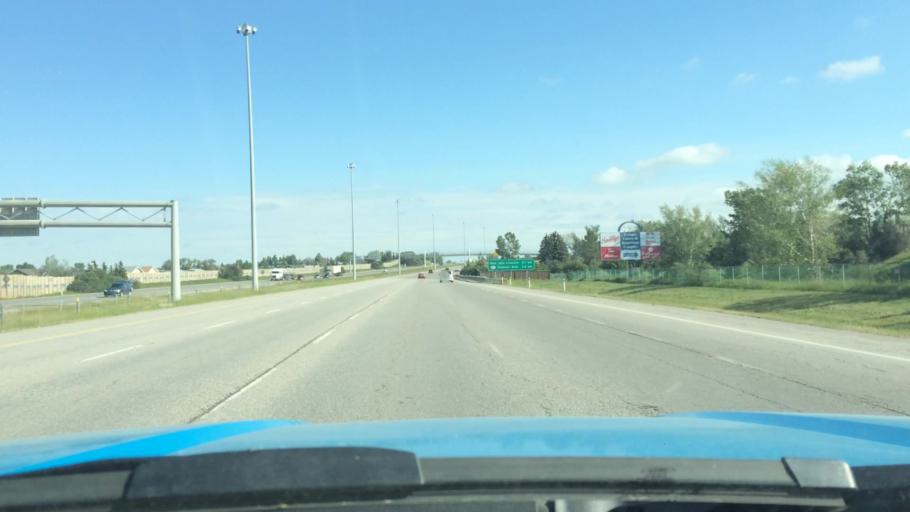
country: CA
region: Alberta
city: Airdrie
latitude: 51.2766
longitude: -114.0015
